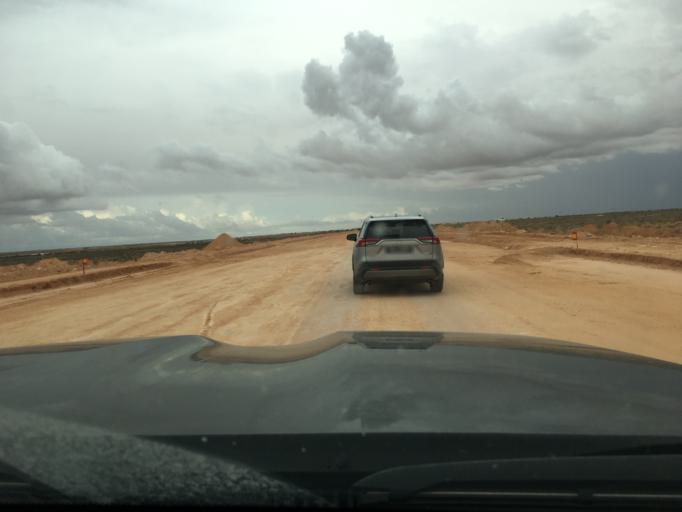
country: TN
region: Madanin
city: Medenine
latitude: 33.2802
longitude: 10.5944
